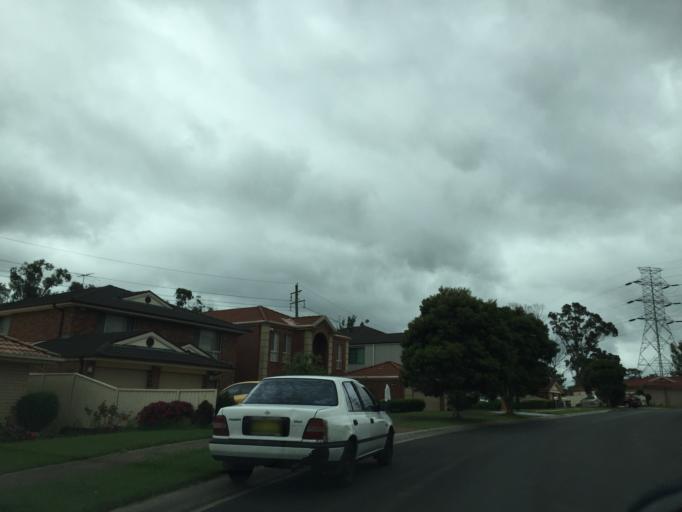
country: AU
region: New South Wales
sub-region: Blacktown
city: Blacktown
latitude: -33.7926
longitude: 150.8987
